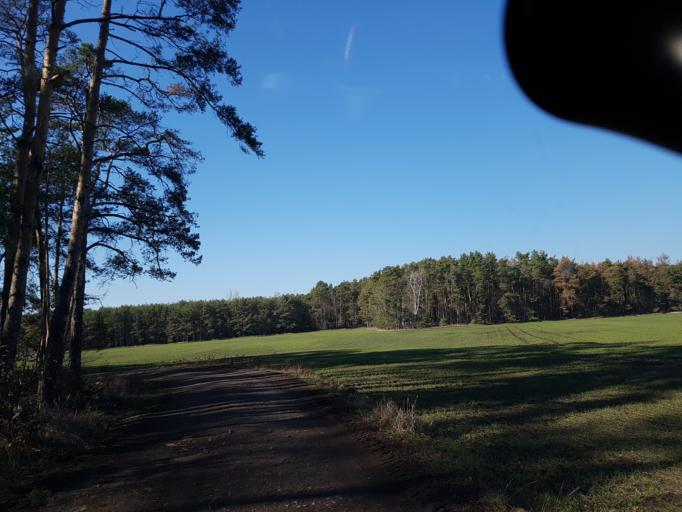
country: DE
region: Brandenburg
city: Trobitz
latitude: 51.5442
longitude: 13.4577
